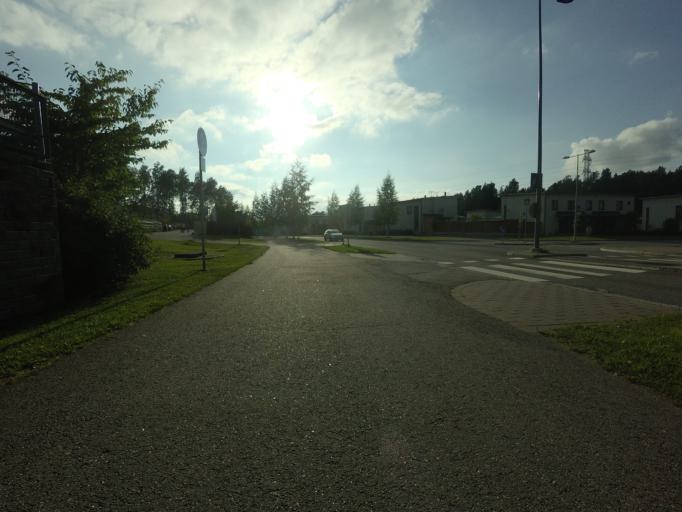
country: FI
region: Uusimaa
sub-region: Helsinki
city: Espoo
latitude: 60.1657
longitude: 24.6383
